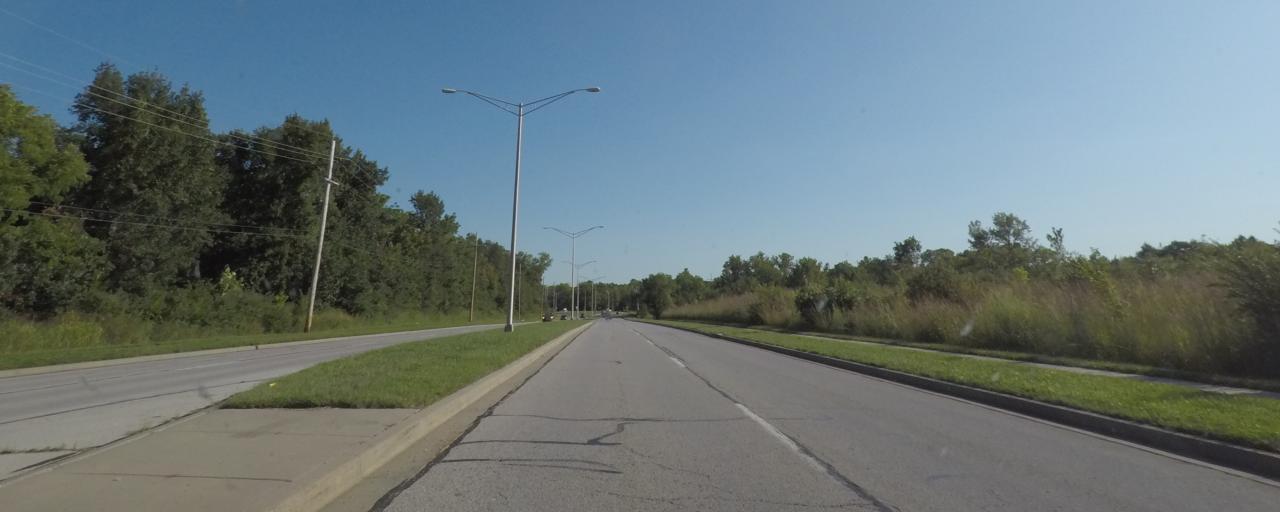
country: US
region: Missouri
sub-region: Clay County
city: Pleasant Valley
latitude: 39.2345
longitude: -94.4702
